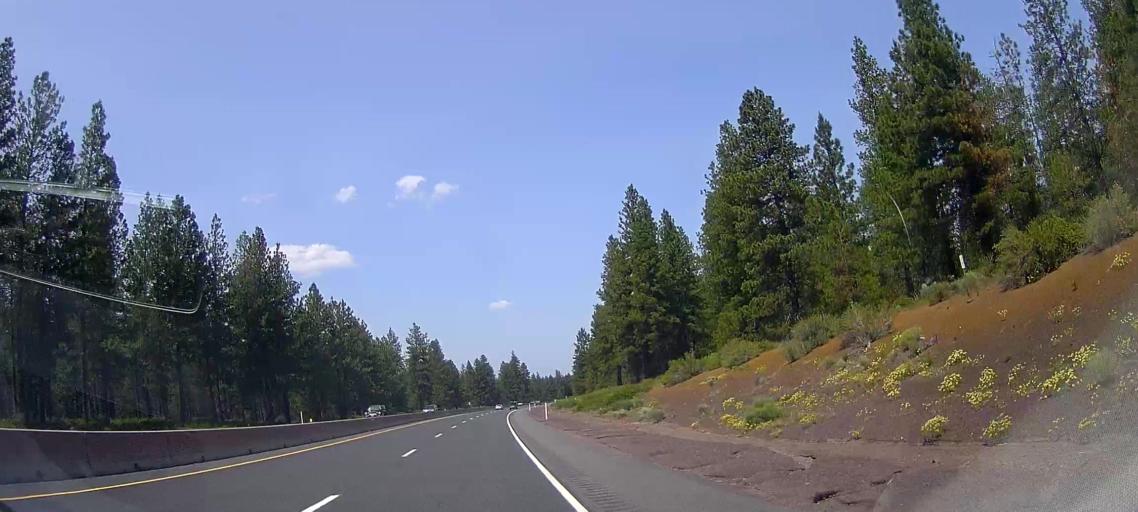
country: US
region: Oregon
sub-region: Deschutes County
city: Deschutes River Woods
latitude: 43.9257
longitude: -121.3521
